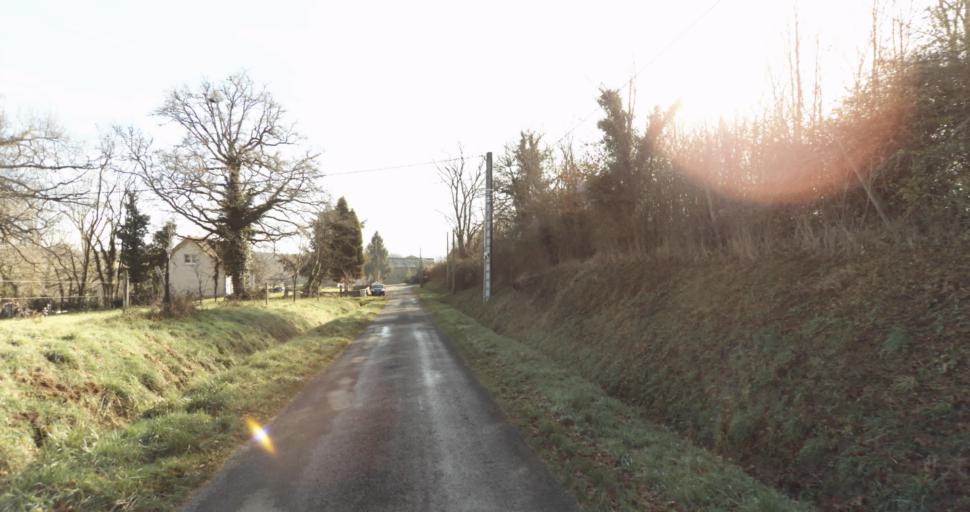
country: FR
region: Limousin
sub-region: Departement de la Haute-Vienne
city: Aixe-sur-Vienne
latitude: 45.7836
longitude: 1.1287
